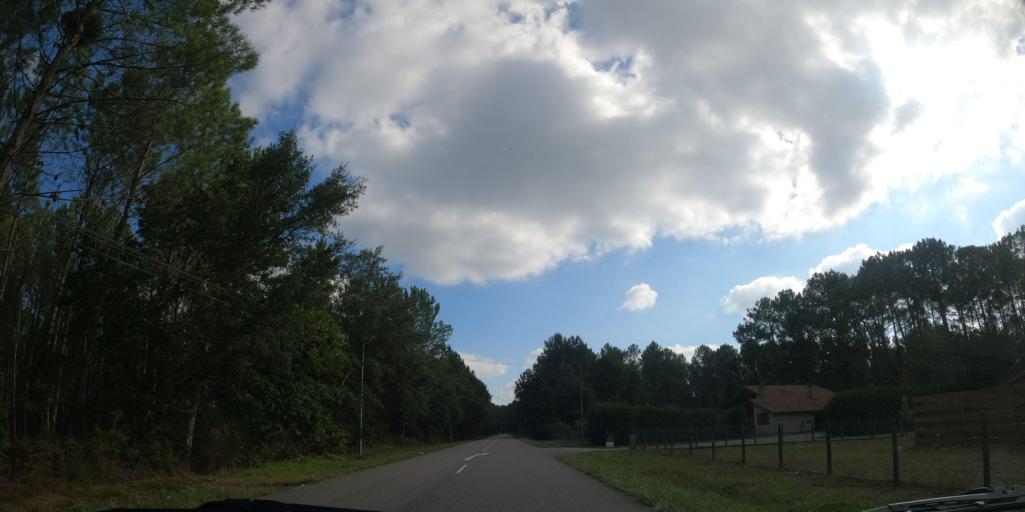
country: FR
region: Aquitaine
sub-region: Departement des Landes
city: Soustons
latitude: 43.7398
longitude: -1.2973
